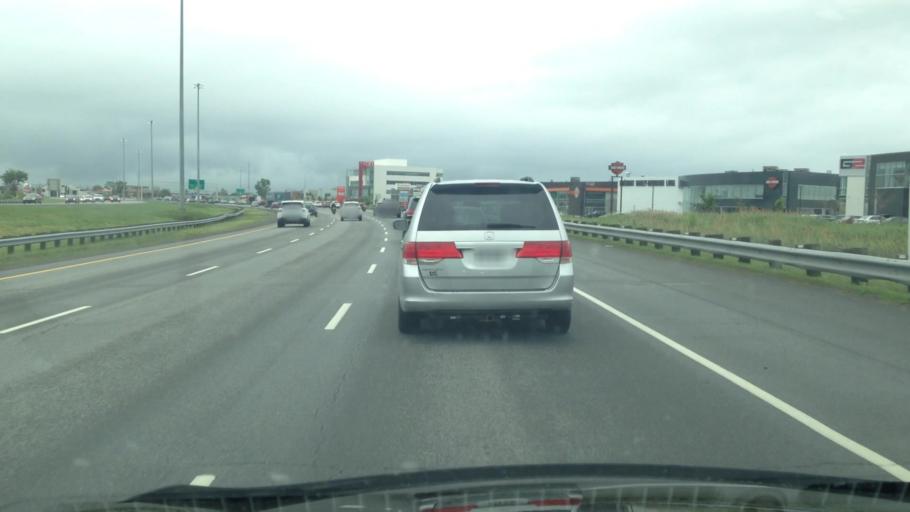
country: CA
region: Quebec
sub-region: Laurentides
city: Rosemere
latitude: 45.5796
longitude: -73.7706
